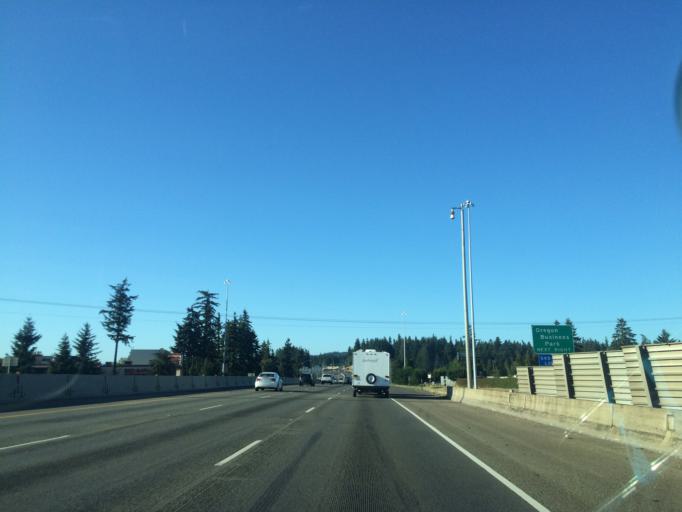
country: US
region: Oregon
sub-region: Washington County
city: Durham
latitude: 45.3960
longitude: -122.7469
